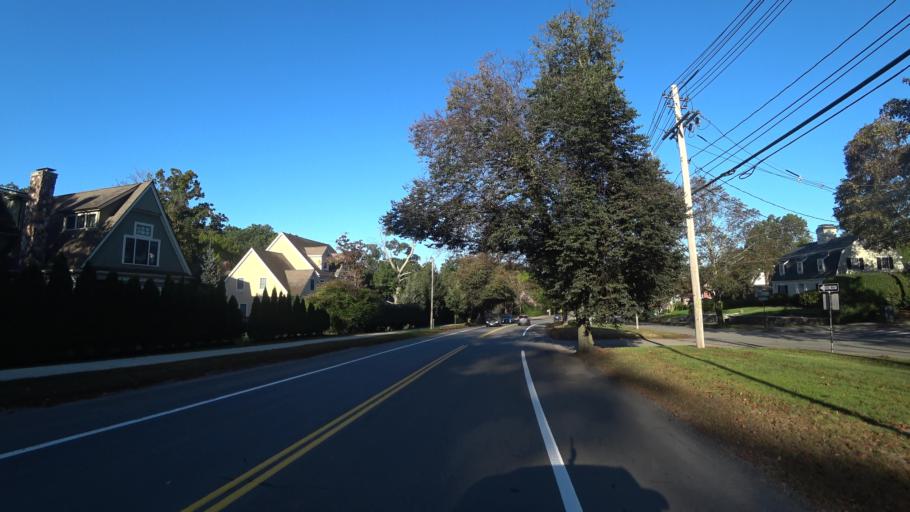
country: US
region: Massachusetts
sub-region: Middlesex County
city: Newton
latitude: 42.3396
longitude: -71.2356
